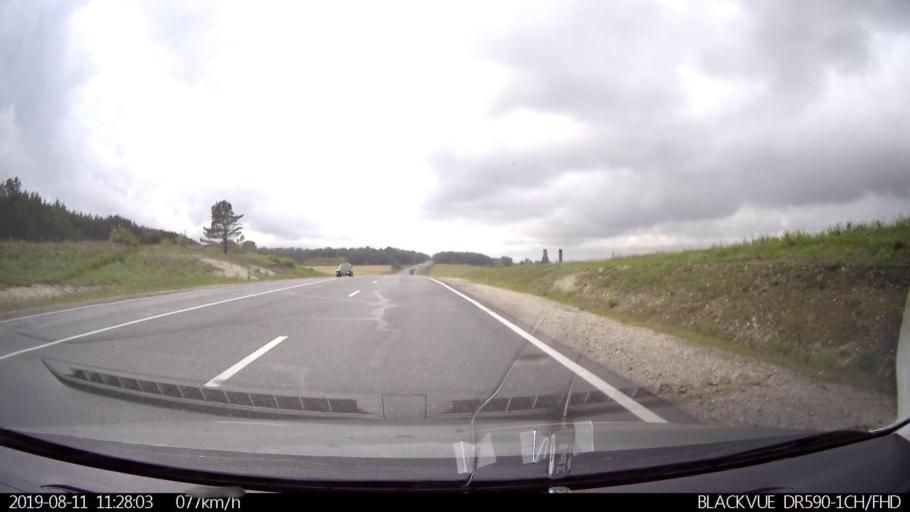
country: RU
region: Ulyanovsk
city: Krasnyy Gulyay
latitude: 54.0847
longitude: 48.2297
